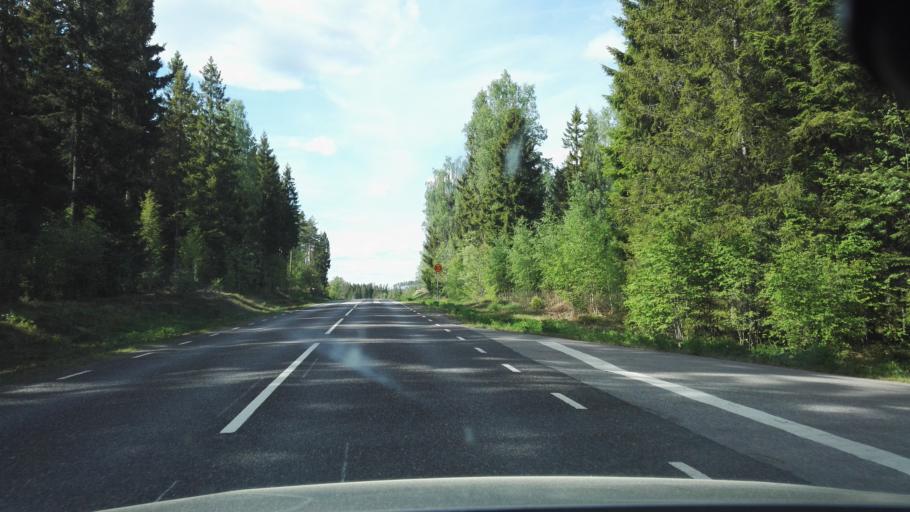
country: SE
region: Kronoberg
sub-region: Vaxjo Kommun
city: Braas
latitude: 57.0934
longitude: 14.9958
